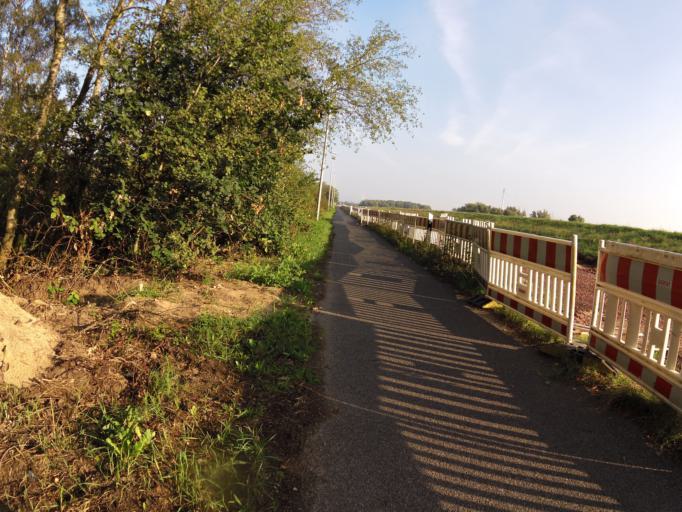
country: DE
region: Lower Saxony
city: Stuhr
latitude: 53.0956
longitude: 8.7285
